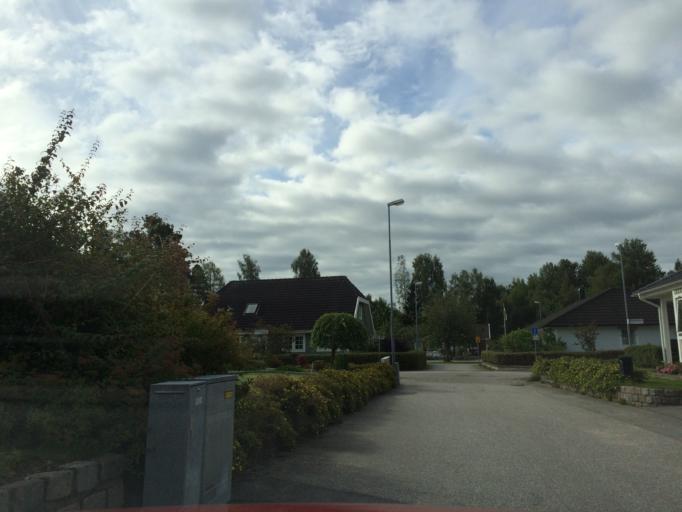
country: SE
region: Vaestra Goetaland
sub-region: Trollhattan
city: Trollhattan
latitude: 58.3229
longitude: 12.2724
